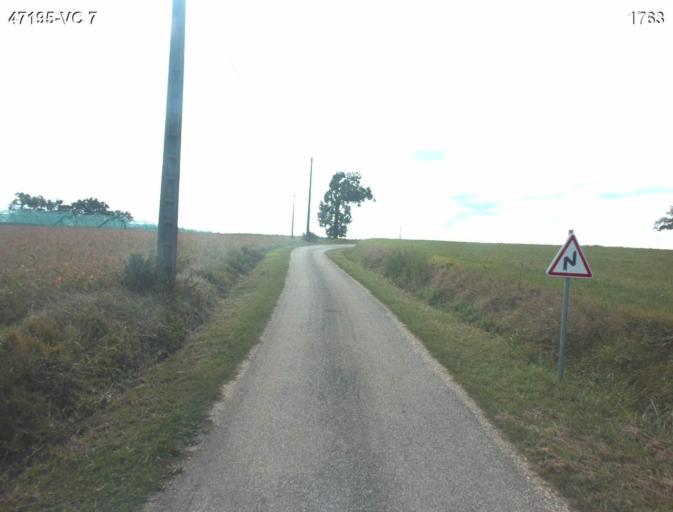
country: FR
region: Aquitaine
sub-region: Departement du Lot-et-Garonne
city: Nerac
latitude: 44.1009
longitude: 0.3403
